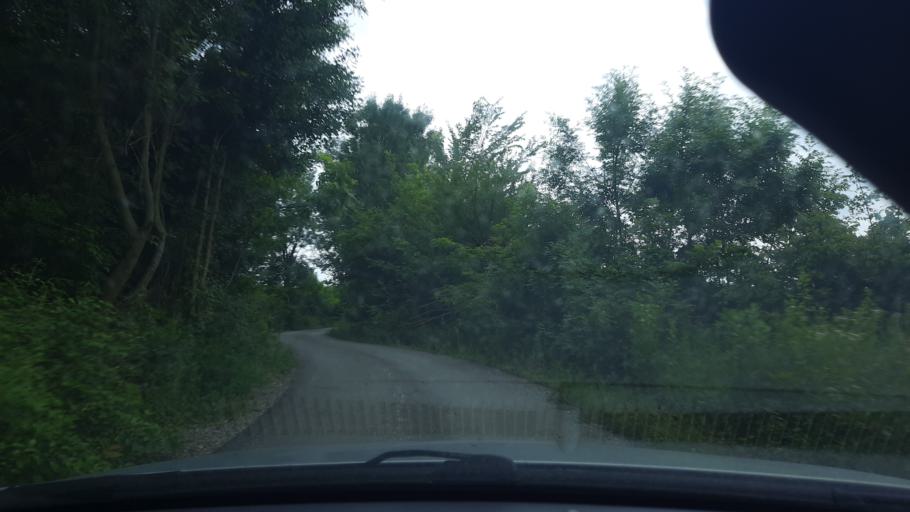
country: RS
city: Jarebice
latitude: 44.5139
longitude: 19.4776
